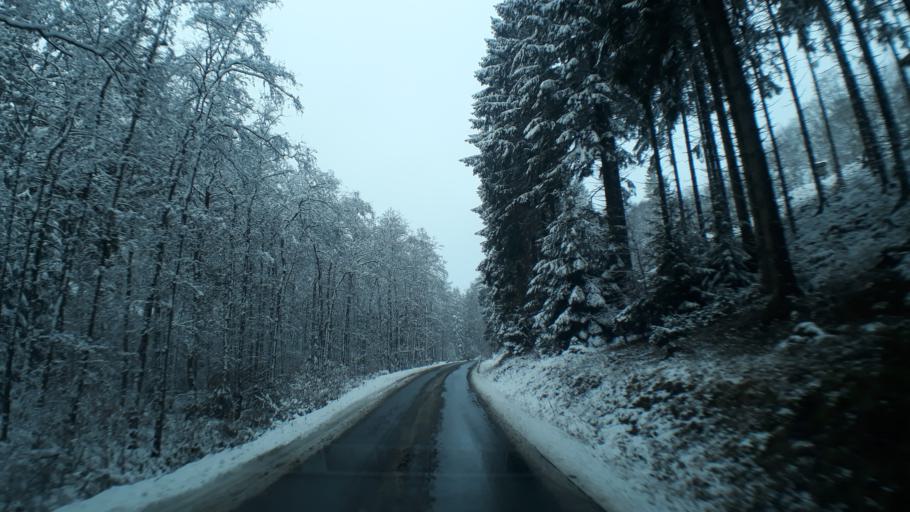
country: DE
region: North Rhine-Westphalia
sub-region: Regierungsbezirk Koln
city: Hurtgenwald
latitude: 50.7377
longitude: 6.2938
